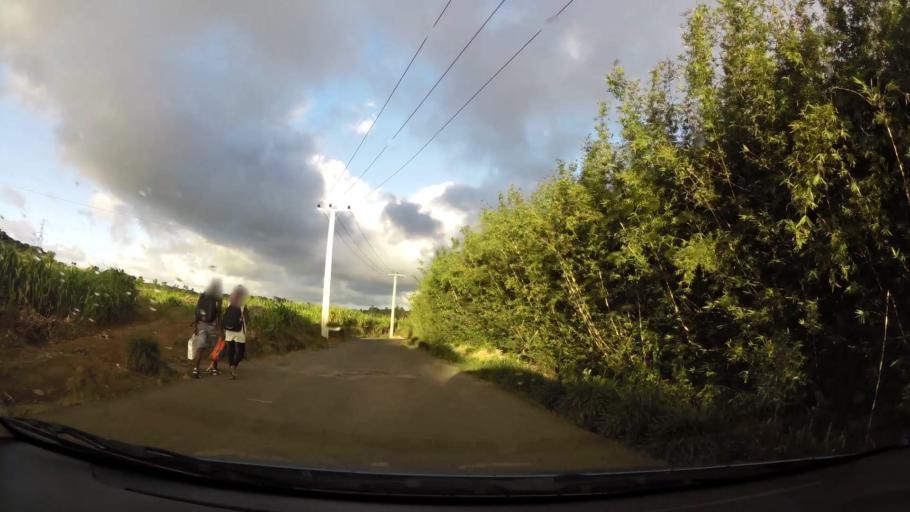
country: MU
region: Plaines Wilhems
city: Curepipe
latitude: -20.3066
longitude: 57.5349
